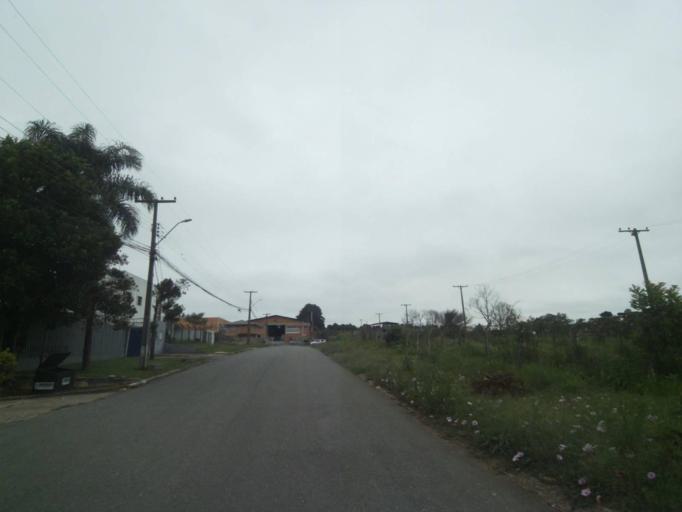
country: BR
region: Parana
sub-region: Araucaria
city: Araucaria
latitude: -25.5466
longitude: -49.3325
